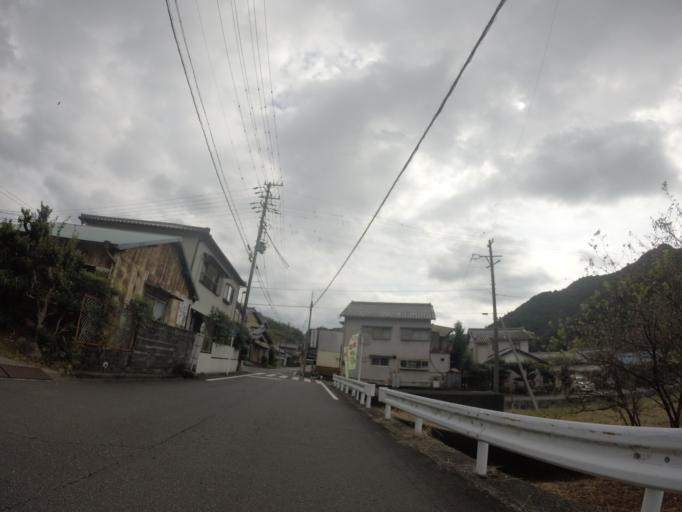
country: JP
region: Shizuoka
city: Fujieda
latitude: 34.9090
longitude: 138.1948
